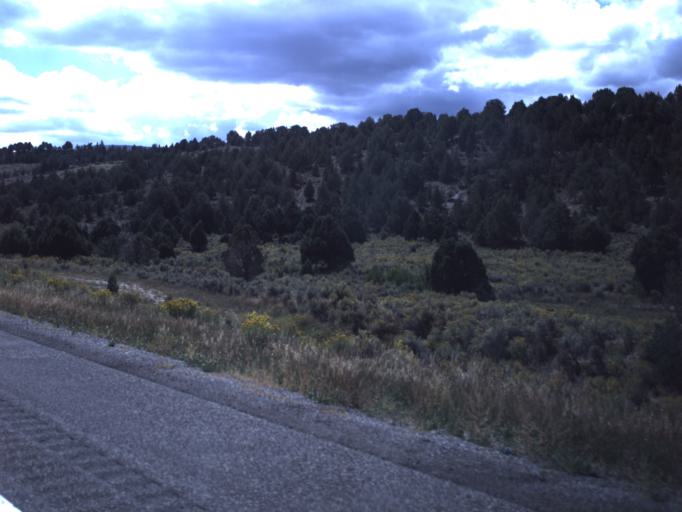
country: US
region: Utah
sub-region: Sevier County
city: Salina
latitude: 38.8557
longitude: -111.5506
